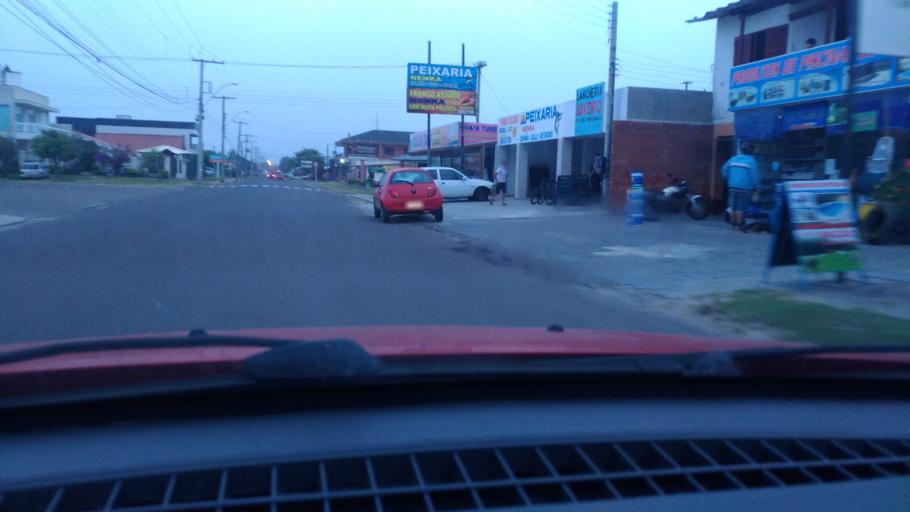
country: BR
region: Rio Grande do Sul
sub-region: Capao Da Canoa
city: Capao da Canoa
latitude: -29.8518
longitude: -50.0652
